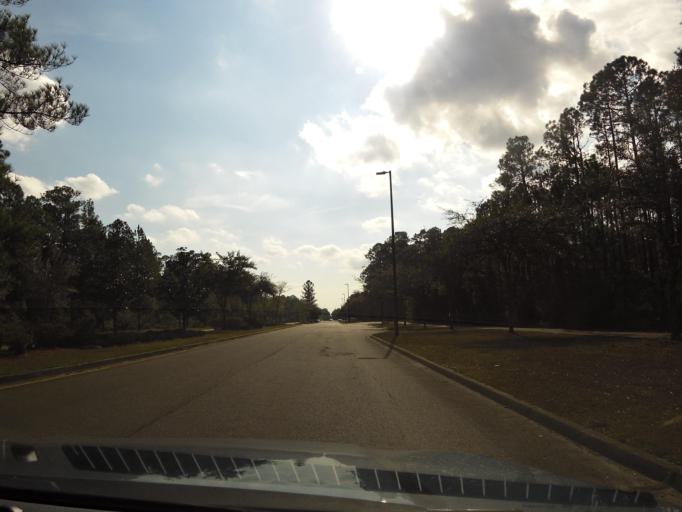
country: US
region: Florida
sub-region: Duval County
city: Baldwin
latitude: 30.2520
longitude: -81.8866
